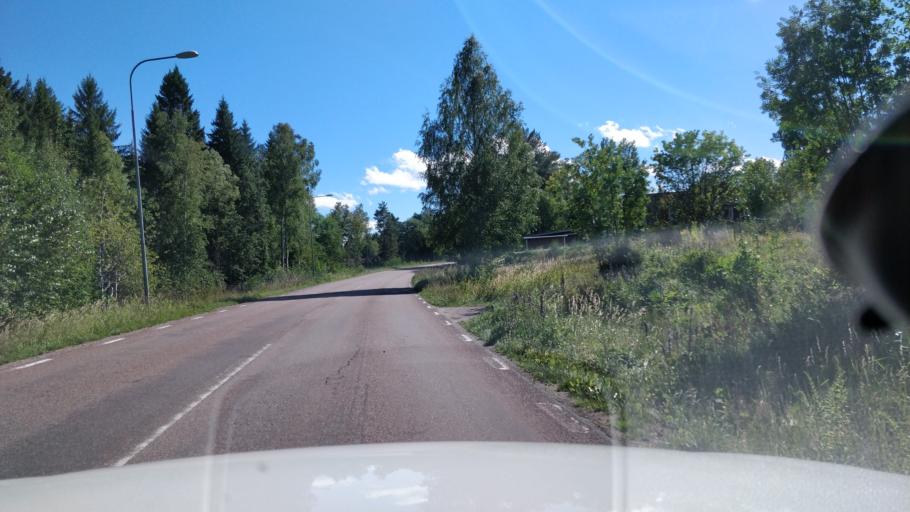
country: SE
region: Dalarna
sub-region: Faluns Kommun
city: Bjursas
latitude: 60.7435
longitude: 15.4690
